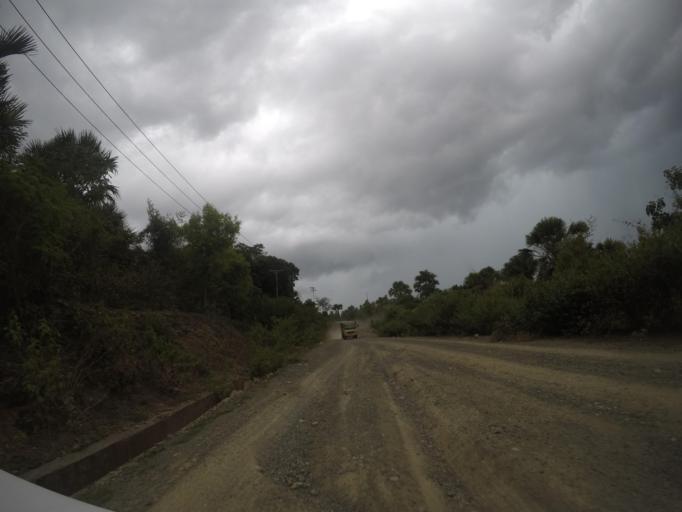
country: TL
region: Bobonaro
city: Maliana
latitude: -8.8497
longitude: 125.0714
